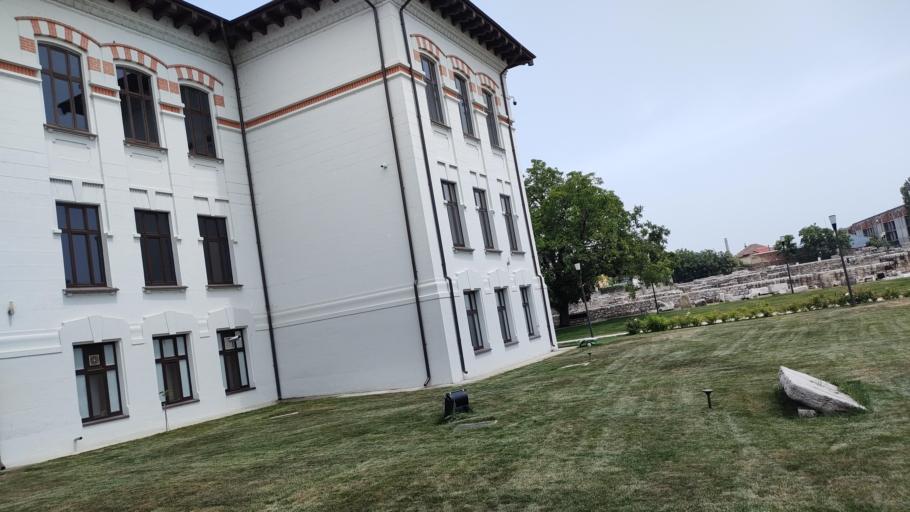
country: RO
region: Mehedinti
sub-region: Municipiul Drobeta-Turnu Severin
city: Drobeta-Turnu Severin
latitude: 44.6247
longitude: 22.6666
